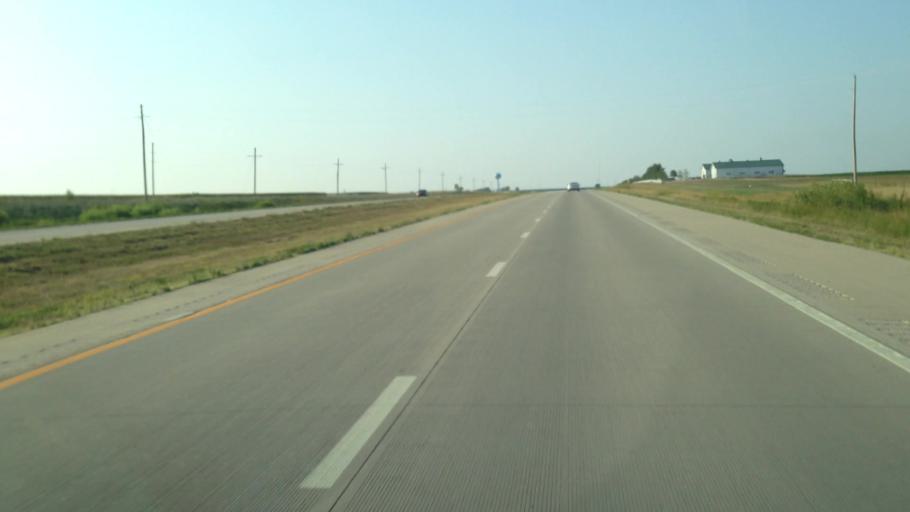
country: US
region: Kansas
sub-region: Douglas County
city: Baldwin City
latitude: 38.8216
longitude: -95.2688
